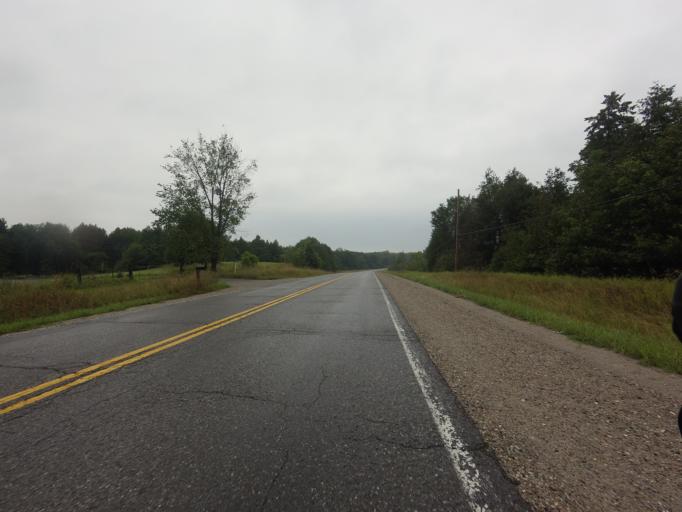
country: CA
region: Ontario
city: Carleton Place
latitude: 45.1380
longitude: -76.3281
